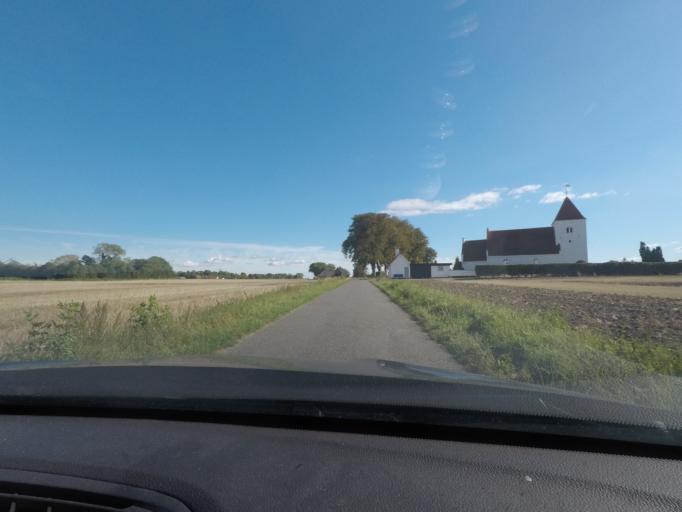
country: DK
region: Zealand
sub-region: Lolland Kommune
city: Maribo
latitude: 54.9735
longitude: 11.5223
